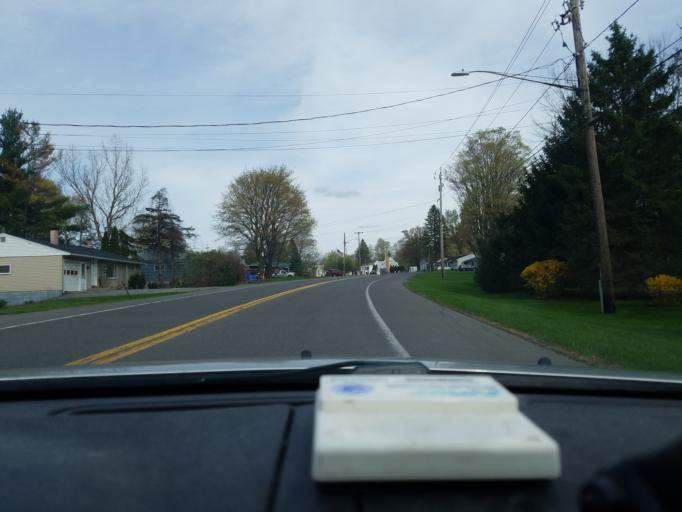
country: US
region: New York
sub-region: Onondaga County
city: North Syracuse
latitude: 43.1424
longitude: -76.1481
